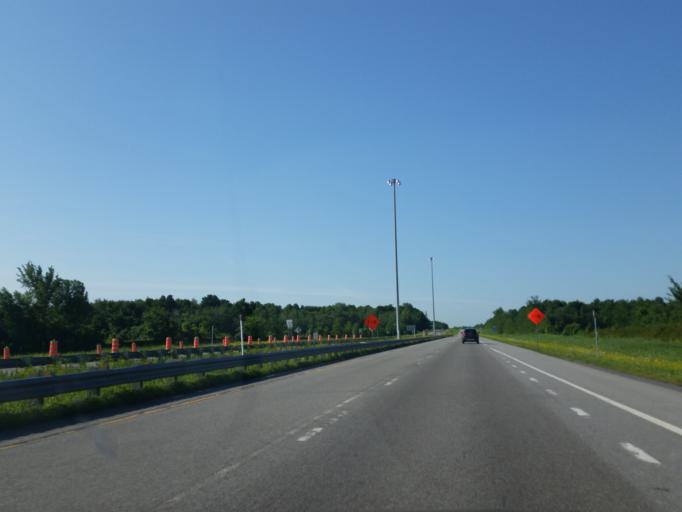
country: CA
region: Quebec
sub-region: Monteregie
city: Napierville
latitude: 45.2642
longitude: -73.4682
